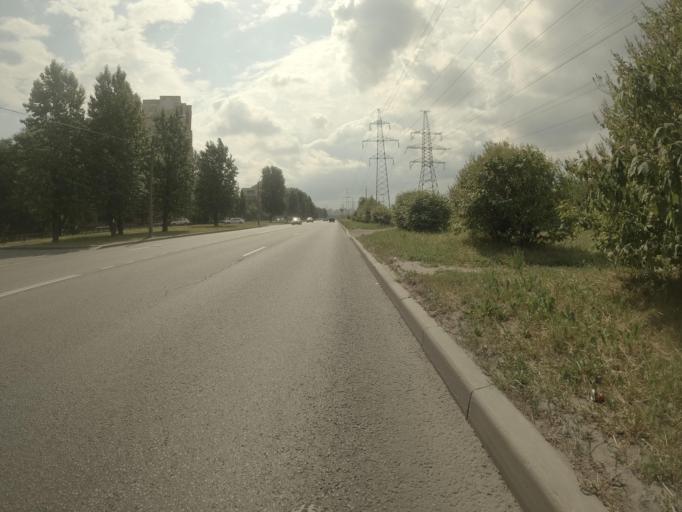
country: RU
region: St.-Petersburg
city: Krasnogvargeisky
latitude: 59.9530
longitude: 30.4605
